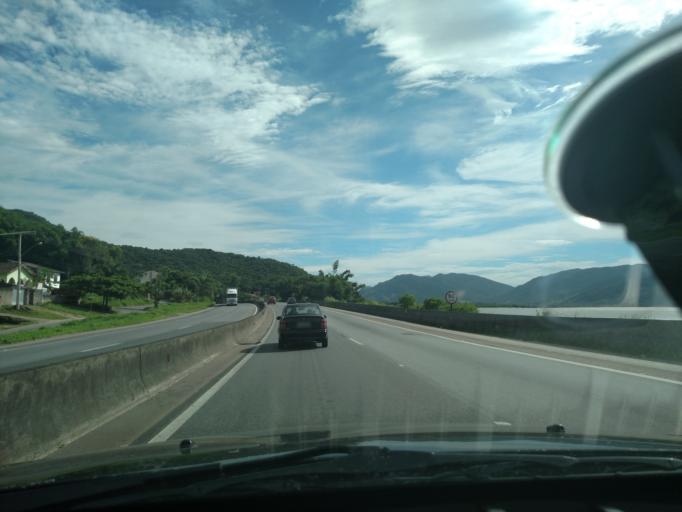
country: BR
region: Santa Catarina
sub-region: Biguacu
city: Biguacu
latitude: -27.4383
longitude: -48.6263
